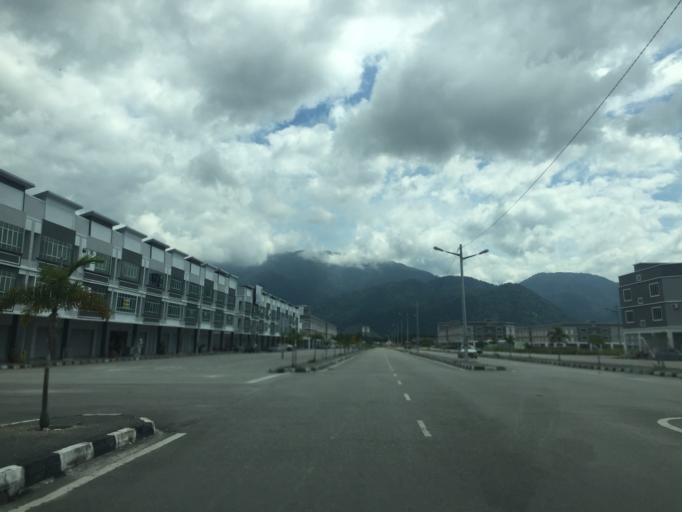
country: MY
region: Perak
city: Kampar
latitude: 4.3236
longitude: 101.1261
